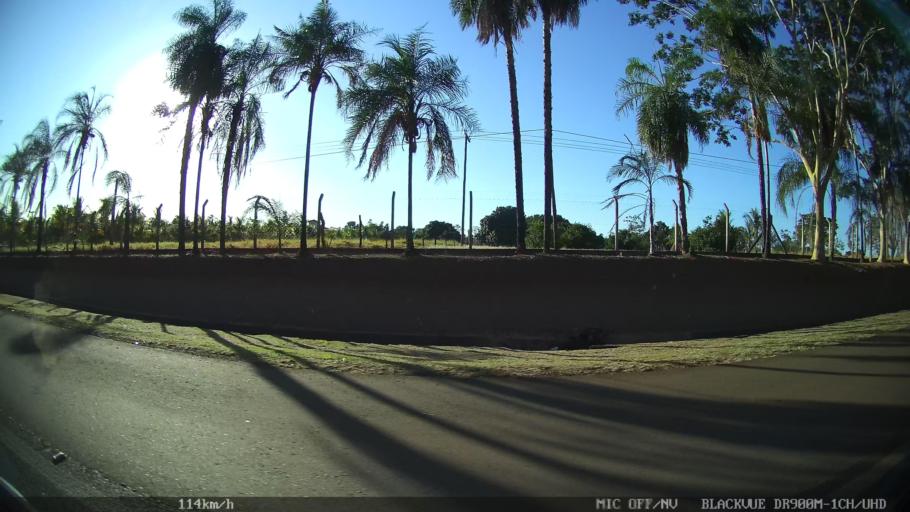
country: BR
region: Sao Paulo
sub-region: Guapiacu
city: Guapiacu
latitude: -20.7873
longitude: -49.2833
